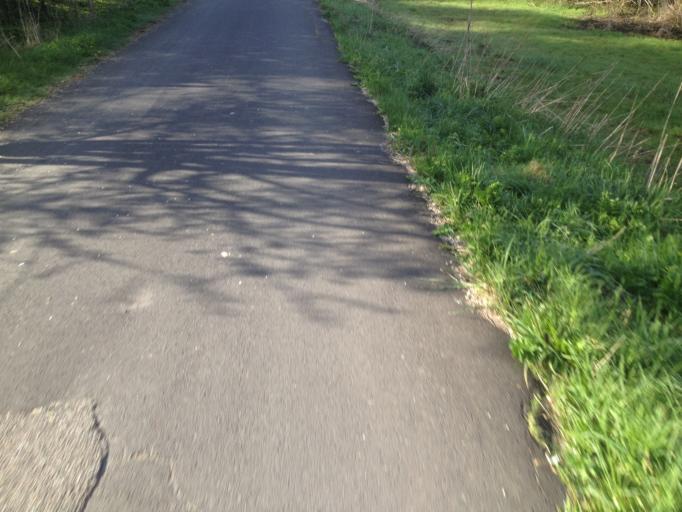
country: DK
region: Capital Region
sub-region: Ballerup Kommune
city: Ballerup
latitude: 55.7426
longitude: 12.3768
